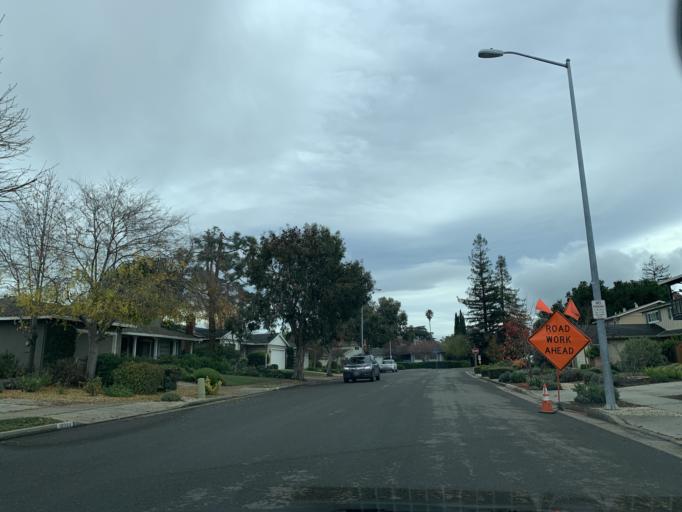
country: US
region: California
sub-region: Santa Clara County
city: Cupertino
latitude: 37.3275
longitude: -122.0545
